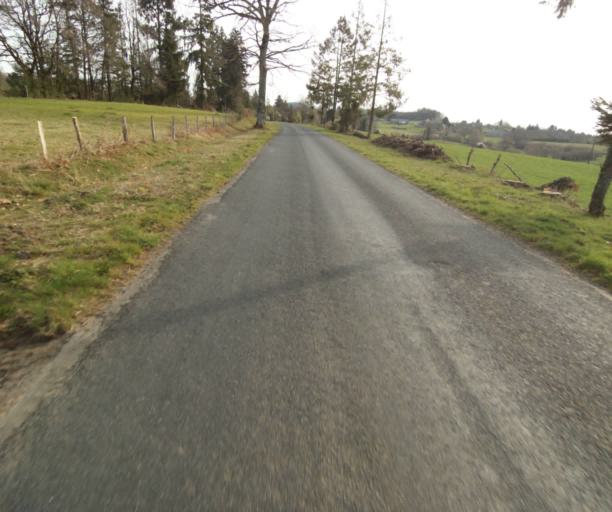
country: FR
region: Limousin
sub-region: Departement de la Correze
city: Chamboulive
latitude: 45.4354
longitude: 1.7723
